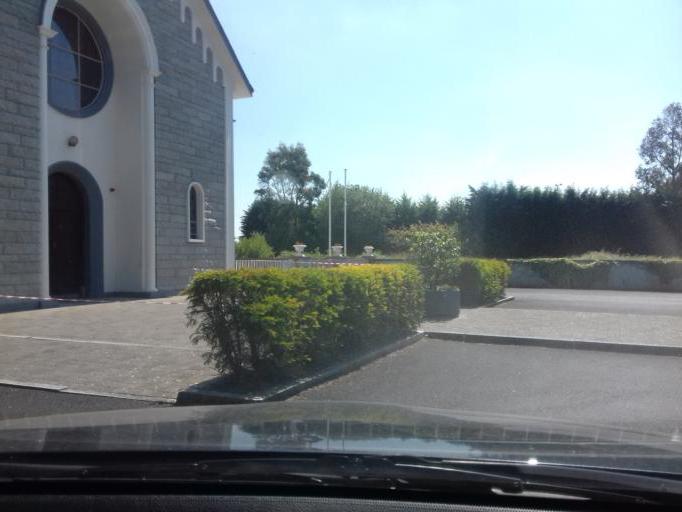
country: IE
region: Leinster
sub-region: An Mhi
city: Ashbourne
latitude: 53.5230
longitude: -6.3149
